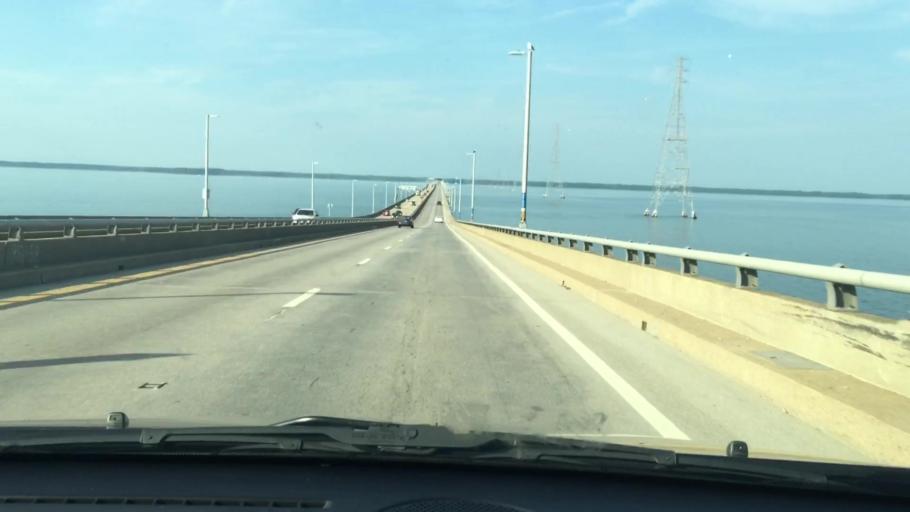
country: US
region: Virginia
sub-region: City of Newport News
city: Newport News
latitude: 37.0008
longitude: -76.4713
